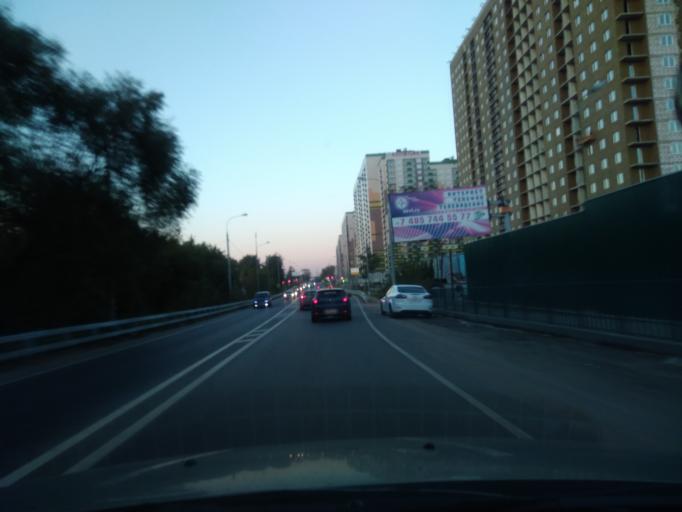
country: RU
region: Moscow
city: Khimki
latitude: 55.8660
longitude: 37.3933
